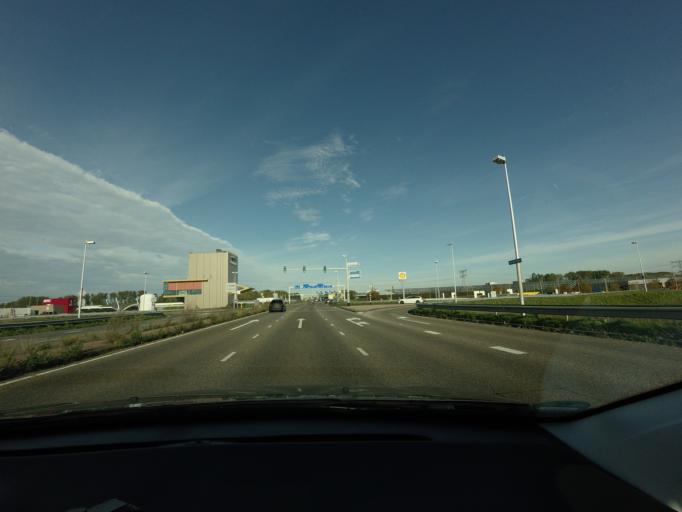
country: NL
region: Utrecht
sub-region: Stichtse Vecht
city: Maarssen
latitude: 52.1155
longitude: 5.0311
